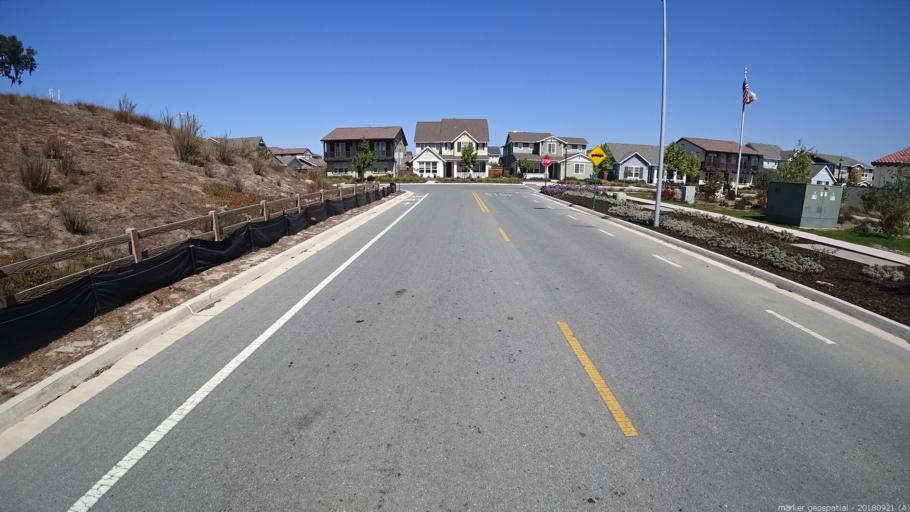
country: US
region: California
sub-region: Monterey County
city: Marina
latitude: 36.6550
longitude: -121.7419
